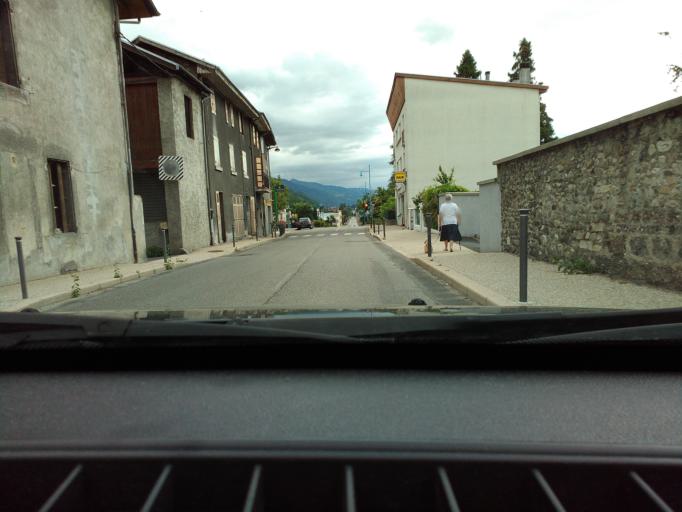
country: FR
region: Rhone-Alpes
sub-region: Departement de l'Isere
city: Froges
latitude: 45.2739
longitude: 5.9250
